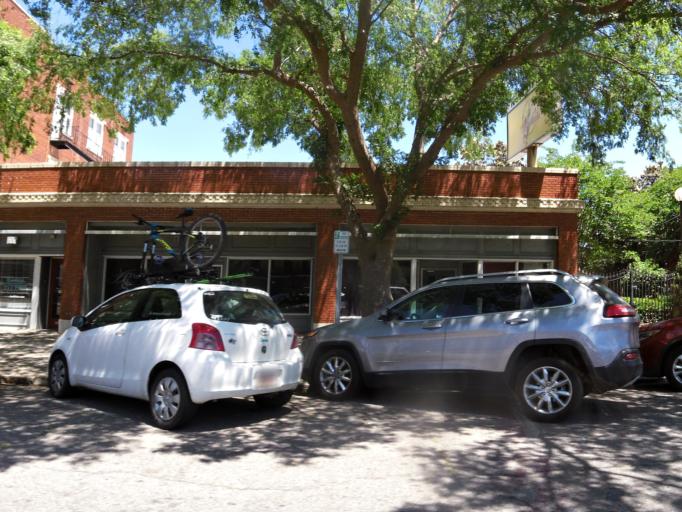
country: US
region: Georgia
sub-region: Richmond County
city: Augusta
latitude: 33.4782
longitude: -81.9737
